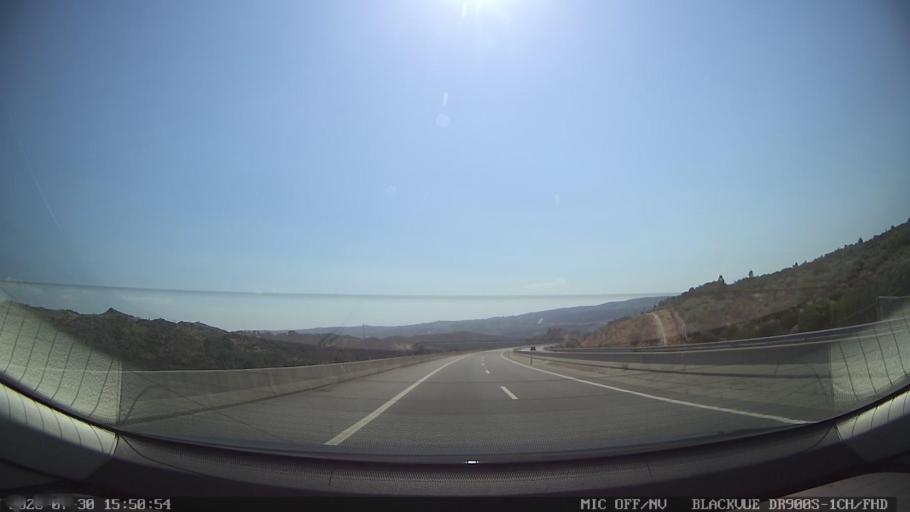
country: PT
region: Vila Real
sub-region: Sabrosa
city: Sabrosa
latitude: 41.3608
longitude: -7.5618
